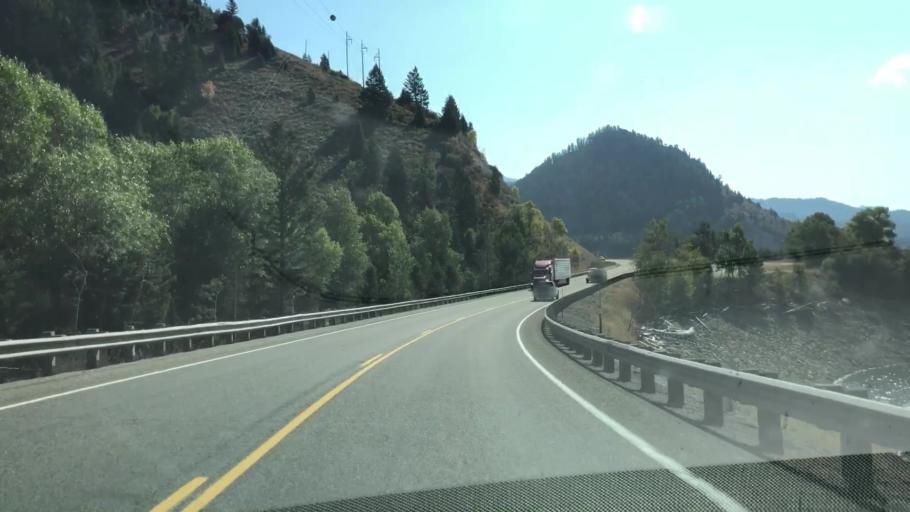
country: US
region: Idaho
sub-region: Teton County
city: Victor
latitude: 43.3203
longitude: -111.1576
